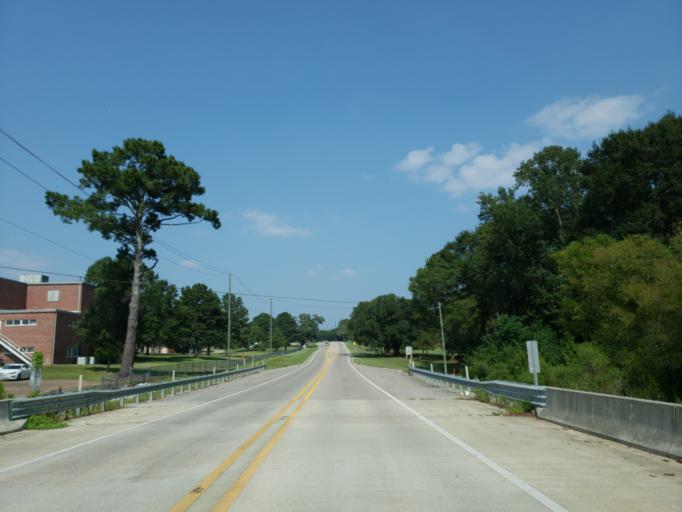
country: US
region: Mississippi
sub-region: Jones County
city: Ellisville
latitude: 31.5847
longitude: -89.2193
